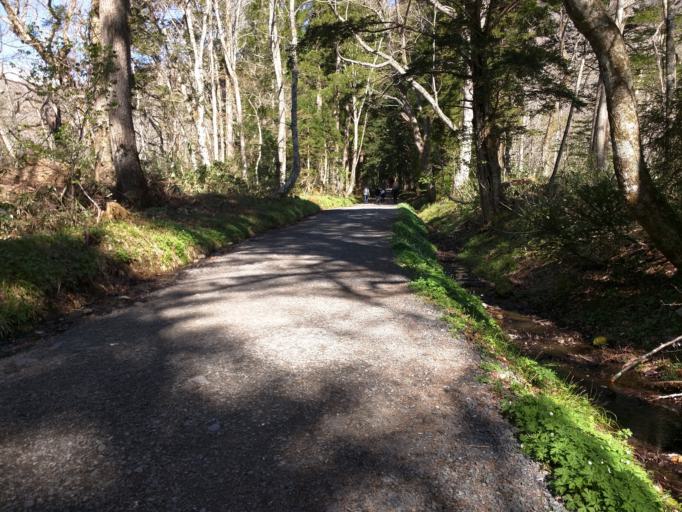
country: JP
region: Nagano
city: Nagano-shi
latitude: 36.7600
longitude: 138.0714
